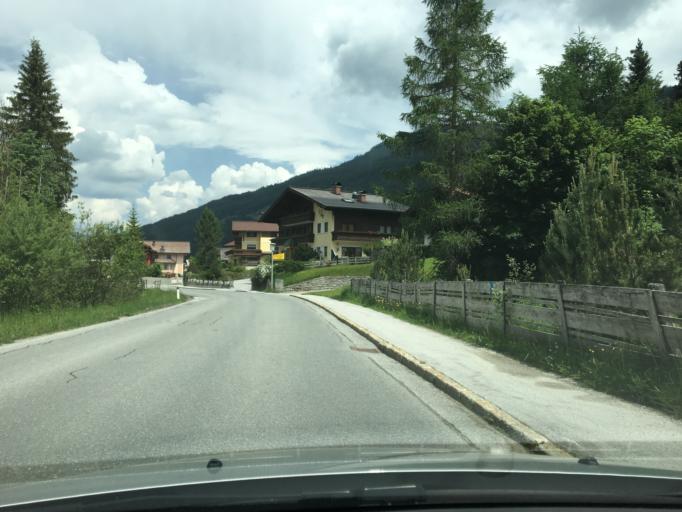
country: AT
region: Salzburg
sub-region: Politischer Bezirk Sankt Johann im Pongau
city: Kleinarl
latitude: 47.2739
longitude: 13.3196
